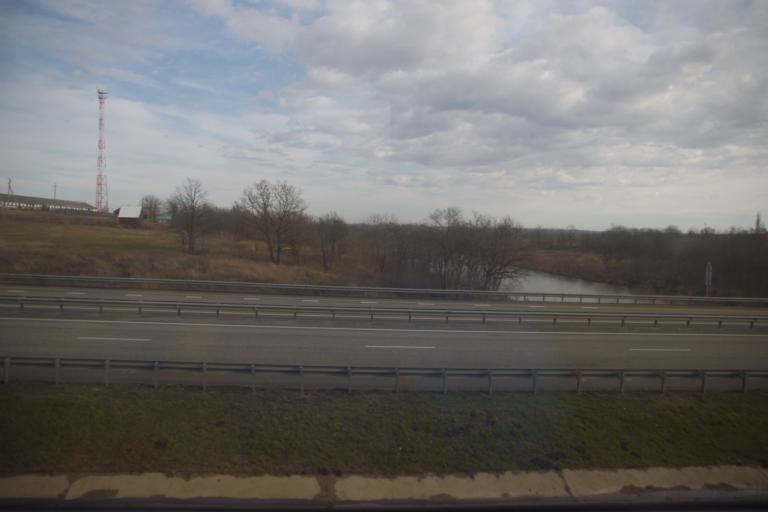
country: RU
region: Adygeya
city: Adygeysk
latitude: 44.8008
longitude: 39.2307
